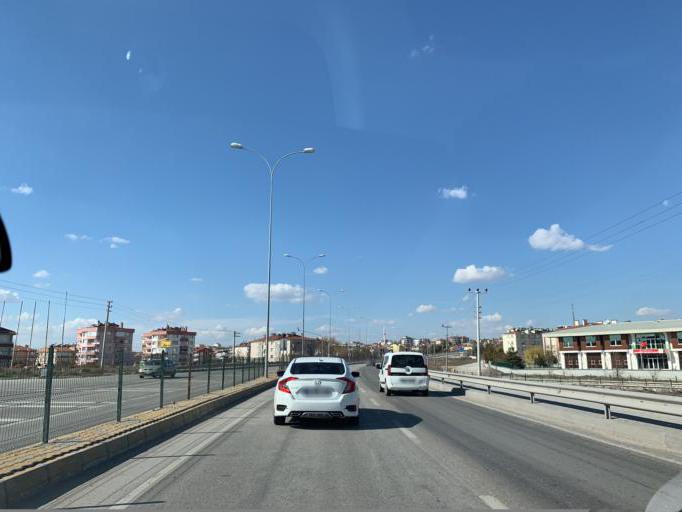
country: TR
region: Konya
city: Cihanbeyli
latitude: 38.6560
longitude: 32.9186
